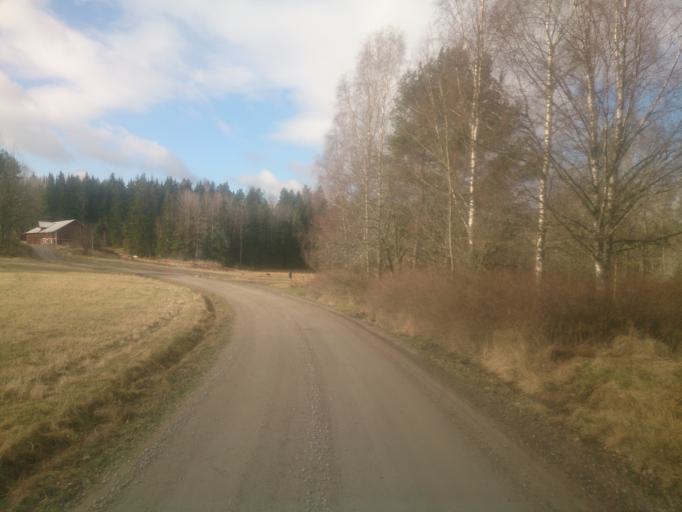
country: SE
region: OEstergoetland
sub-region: Atvidabergs Kommun
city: Atvidaberg
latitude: 58.2287
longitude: 16.1762
